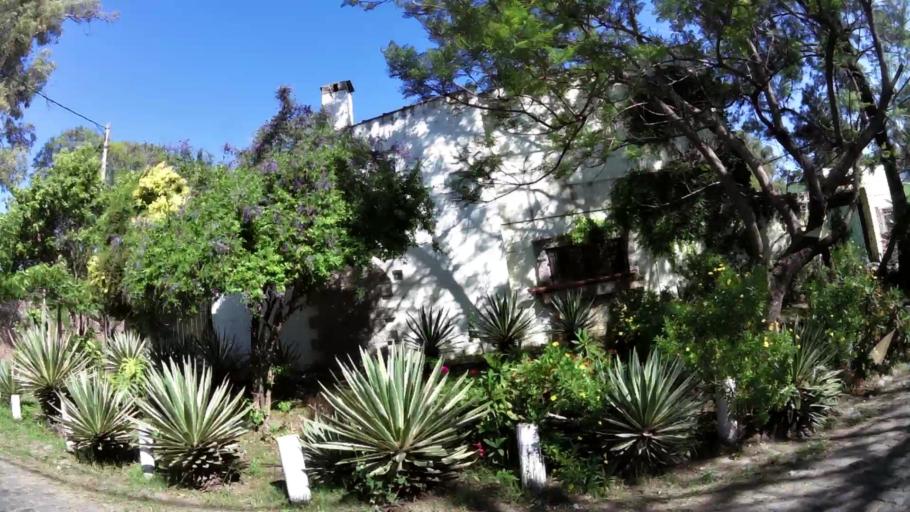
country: AR
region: Buenos Aires
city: Caseros
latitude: -34.5450
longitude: -58.5880
